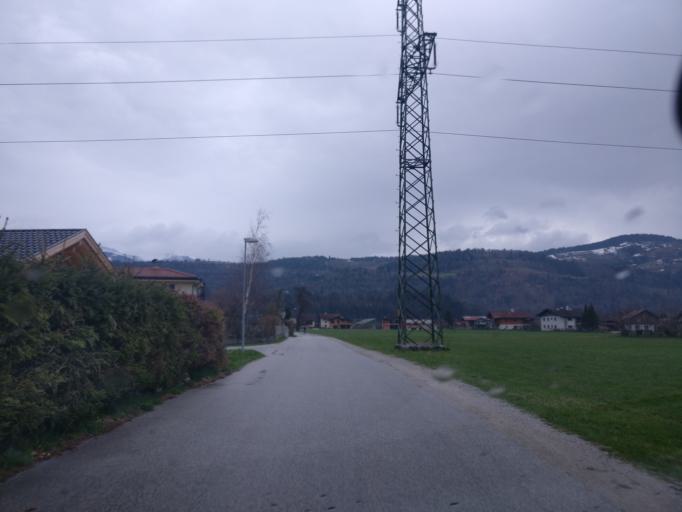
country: AT
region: Salzburg
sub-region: Politischer Bezirk Hallein
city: Kuchl
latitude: 47.6287
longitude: 13.1505
